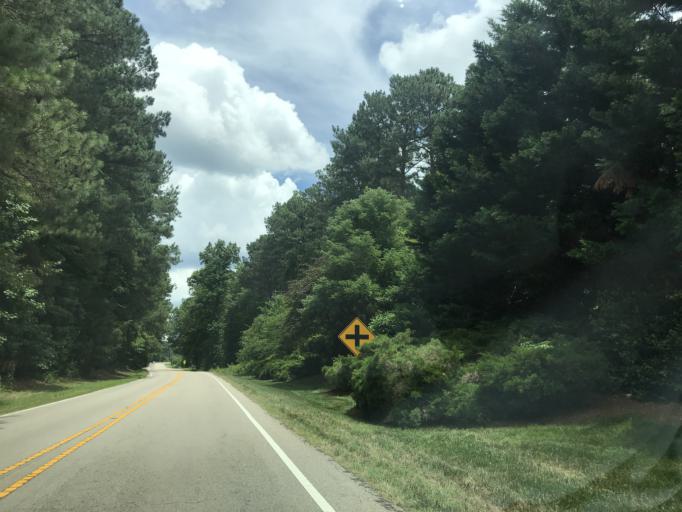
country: US
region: North Carolina
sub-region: Wake County
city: West Raleigh
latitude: 35.9104
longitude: -78.6706
